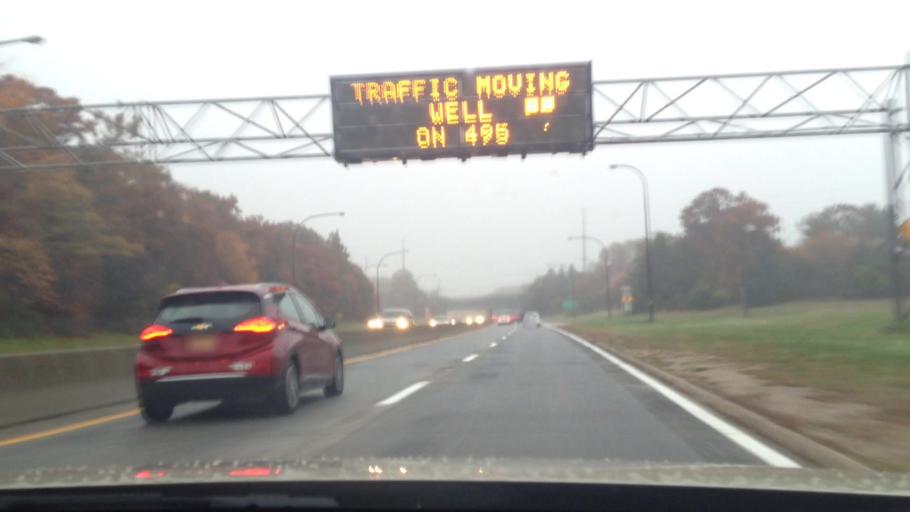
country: US
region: New York
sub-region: Suffolk County
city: Brentwood
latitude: 40.7946
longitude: -73.2785
